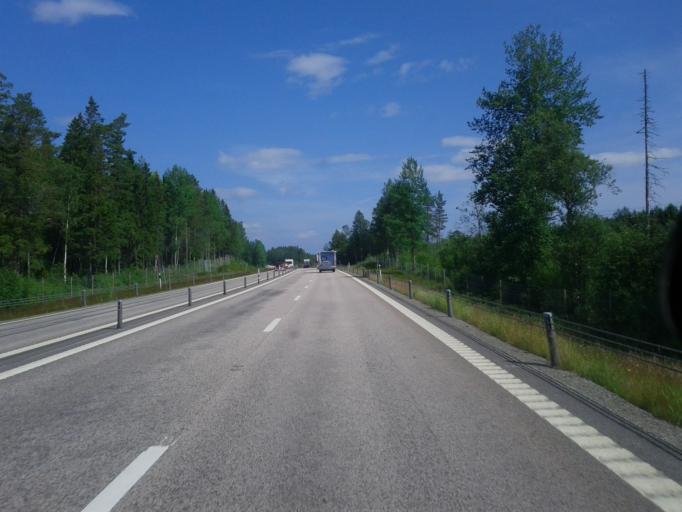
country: SE
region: Vaesterbotten
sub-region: Nordmalings Kommun
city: Nordmaling
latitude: 63.5021
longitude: 19.3394
